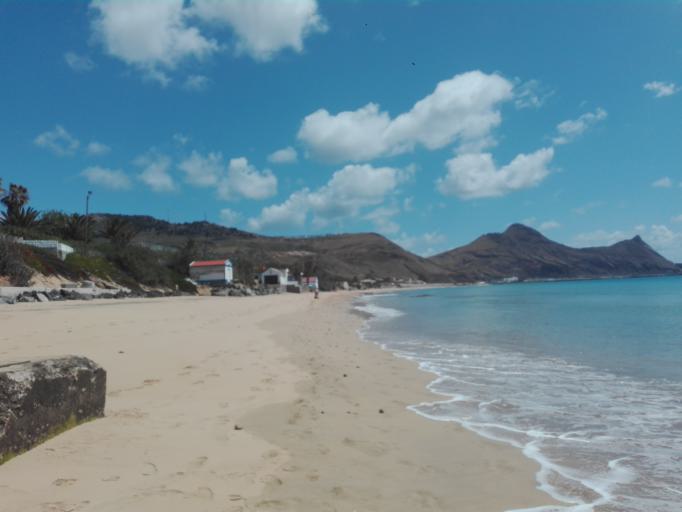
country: PT
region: Madeira
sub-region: Porto Santo
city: Vila de Porto Santo
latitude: 33.0592
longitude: -16.3315
